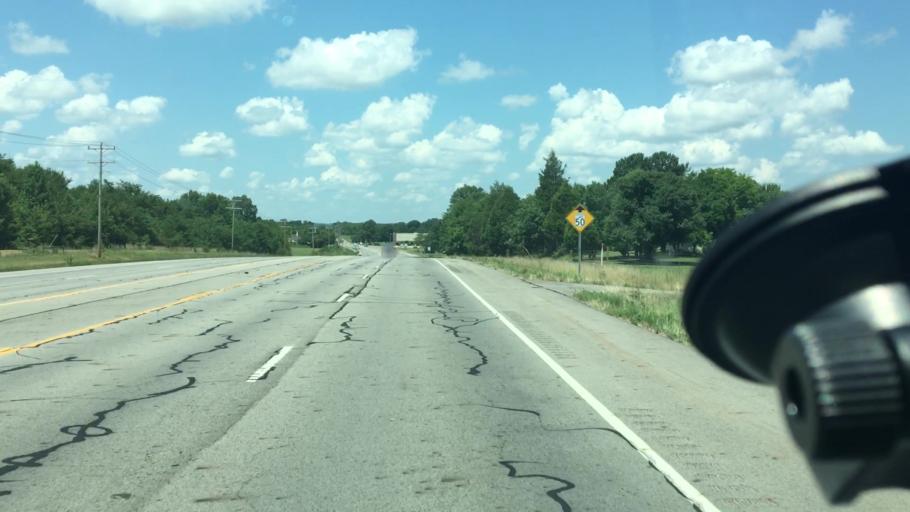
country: US
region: Arkansas
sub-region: Sebastian County
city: Barling
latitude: 35.3198
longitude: -94.2459
